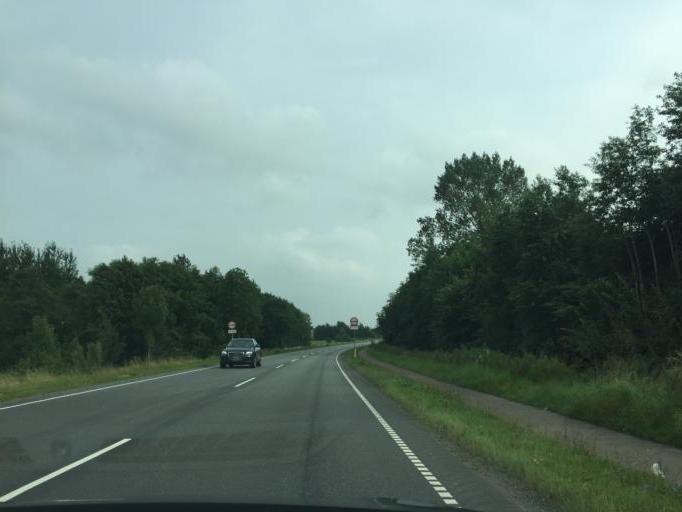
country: DK
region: South Denmark
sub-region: Odense Kommune
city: Hojby
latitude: 55.3251
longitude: 10.4010
